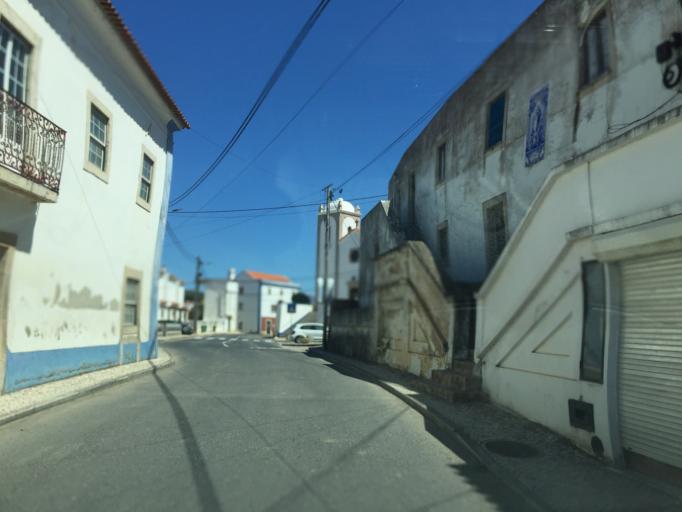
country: PT
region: Lisbon
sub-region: Torres Vedras
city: A dos Cunhados
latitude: 39.1789
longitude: -9.3178
